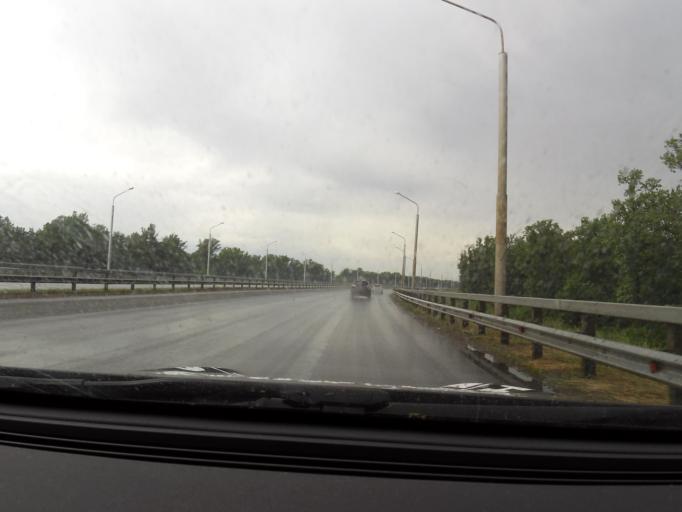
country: RU
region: Bashkortostan
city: Mikhaylovka
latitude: 54.7808
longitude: 55.9181
